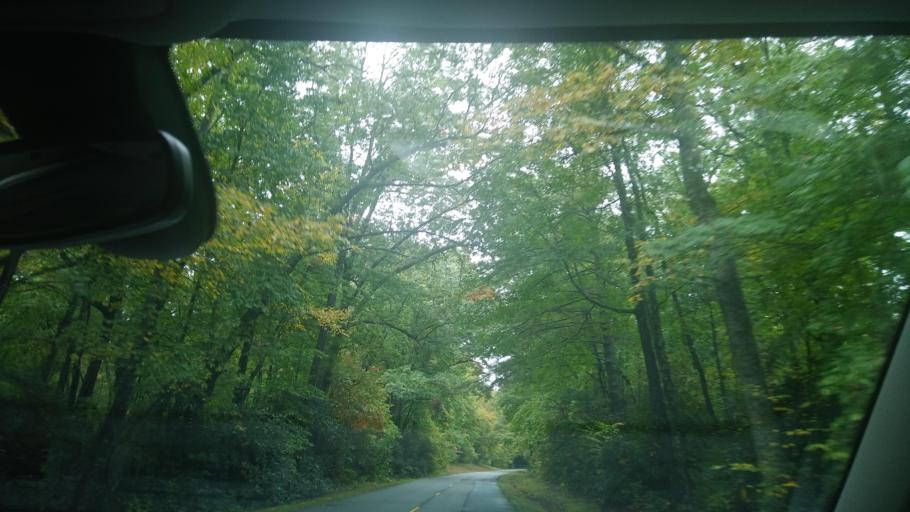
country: US
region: North Carolina
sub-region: Mitchell County
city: Spruce Pine
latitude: 35.8807
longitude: -82.0054
